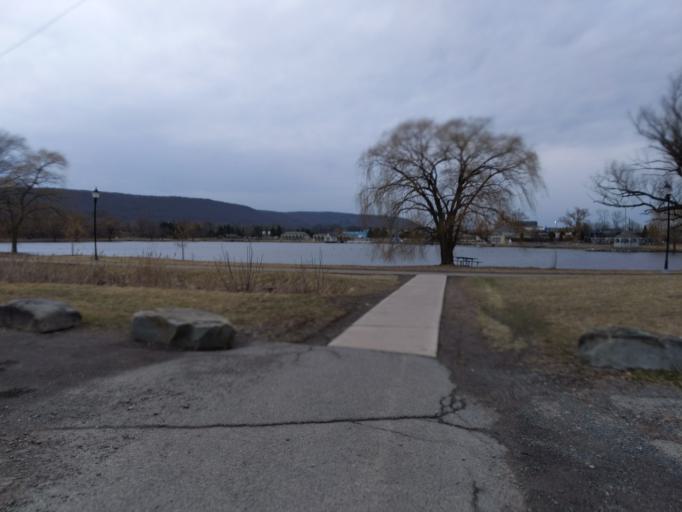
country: US
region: New York
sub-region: Chemung County
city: Elmira Heights
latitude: 42.1126
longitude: -76.8153
